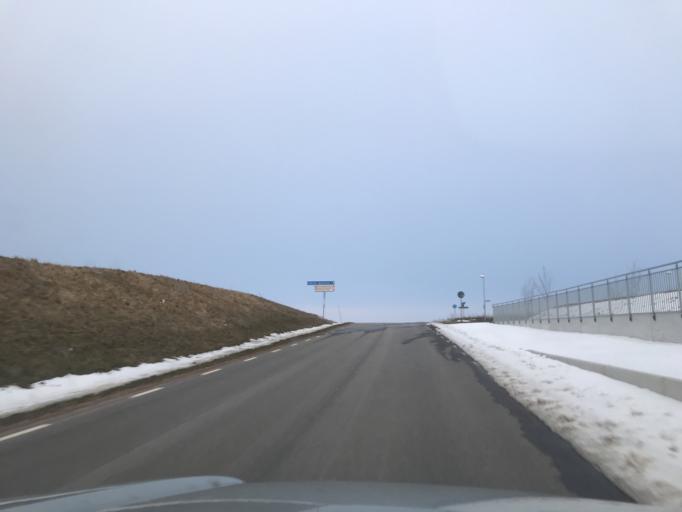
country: SE
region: Skane
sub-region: Malmo
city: Oxie
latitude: 55.4955
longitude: 13.1023
